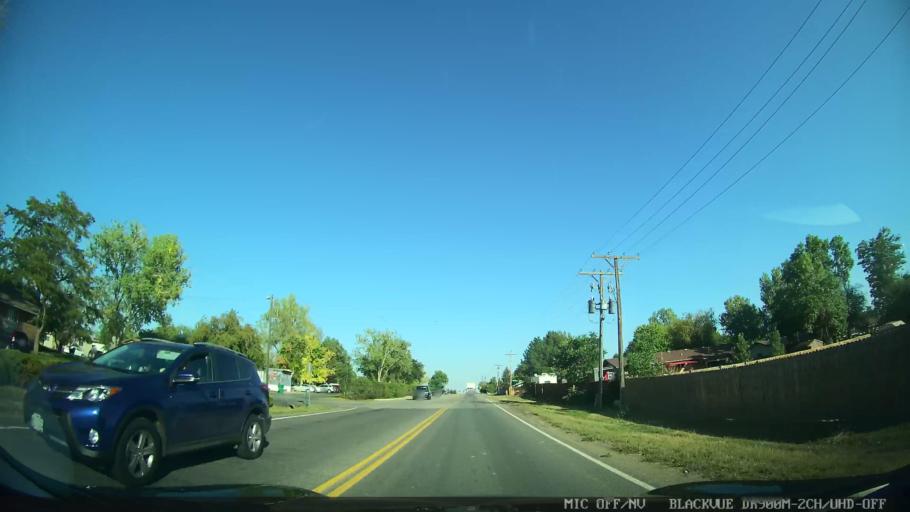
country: US
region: Colorado
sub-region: Larimer County
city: Loveland
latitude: 40.4510
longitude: -105.0826
